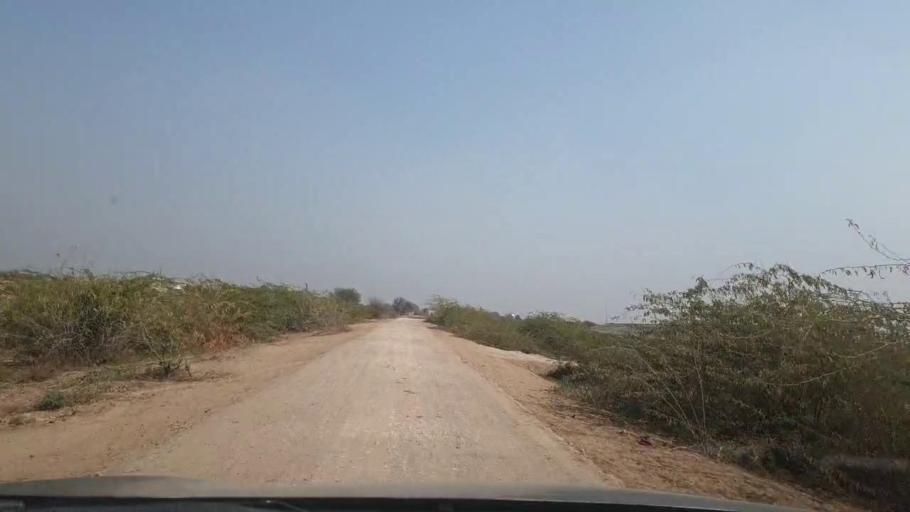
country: PK
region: Sindh
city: Tando Allahyar
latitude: 25.5607
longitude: 68.8352
